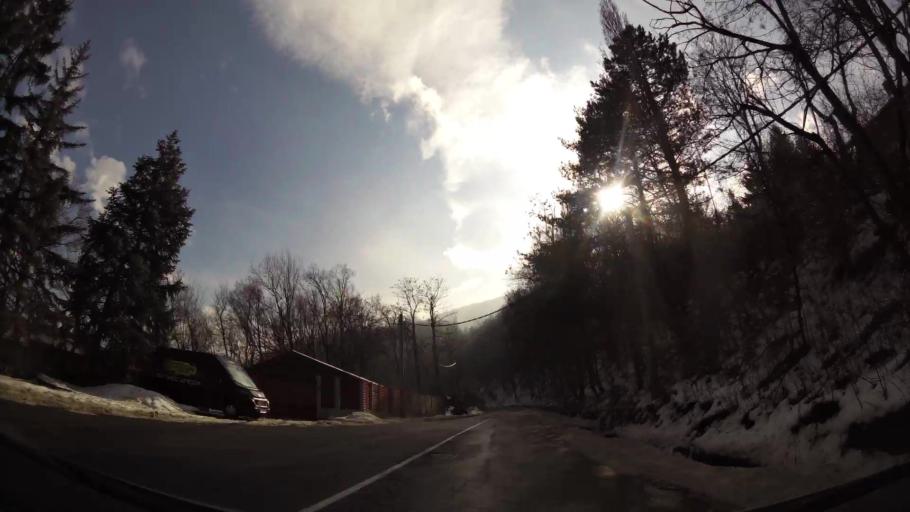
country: BG
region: Sofia-Capital
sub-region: Stolichna Obshtina
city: Sofia
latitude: 42.6471
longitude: 23.2473
